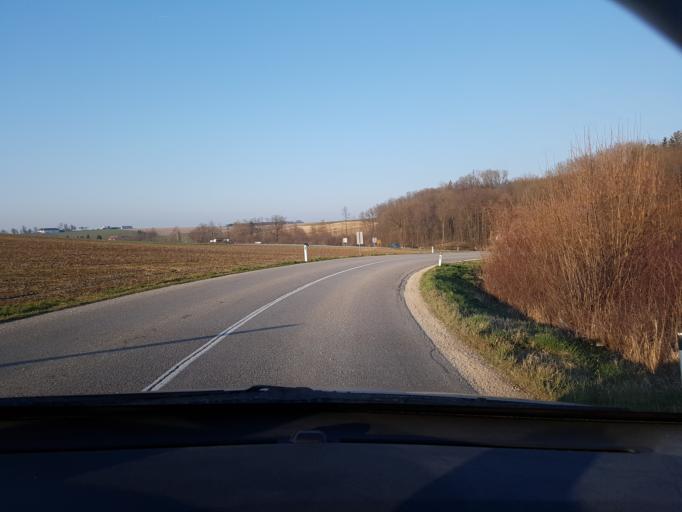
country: AT
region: Upper Austria
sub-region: Politischer Bezirk Steyr-Land
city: Sierning
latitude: 48.1276
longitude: 14.3275
